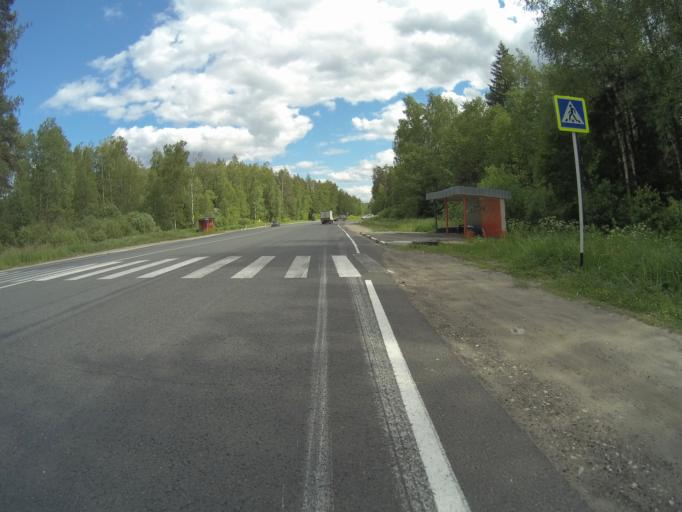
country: RU
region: Vladimir
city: Kommunar
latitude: 56.0197
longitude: 40.5798
